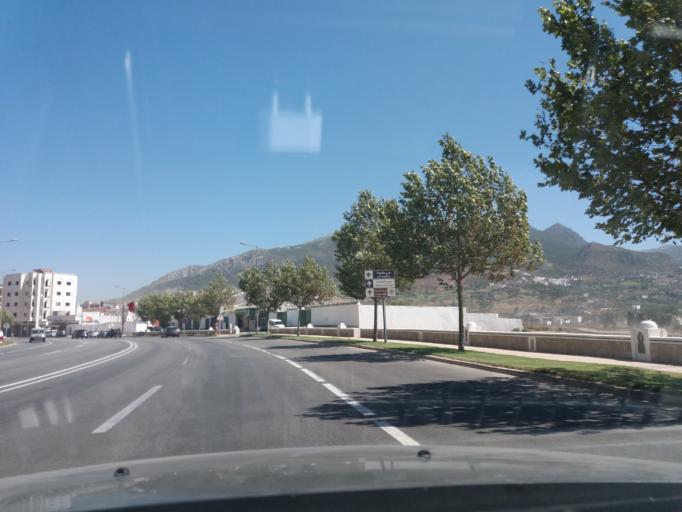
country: MA
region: Tanger-Tetouan
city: Tetouan
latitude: 35.5659
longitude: -5.4025
